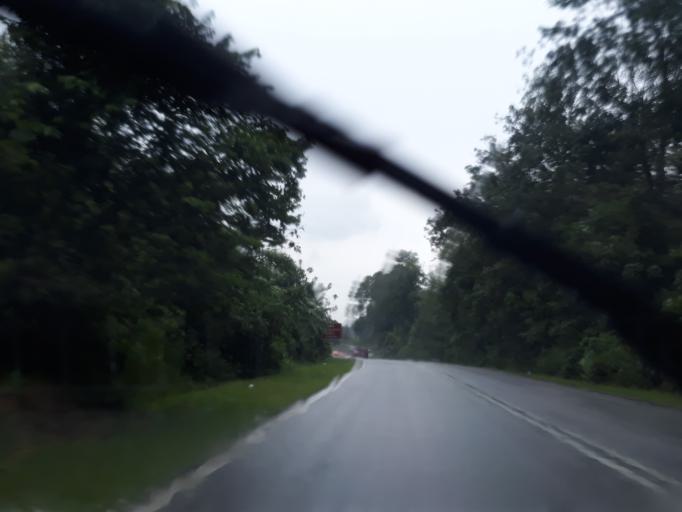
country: MY
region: Kedah
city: Kulim
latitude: 5.3443
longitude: 100.5864
